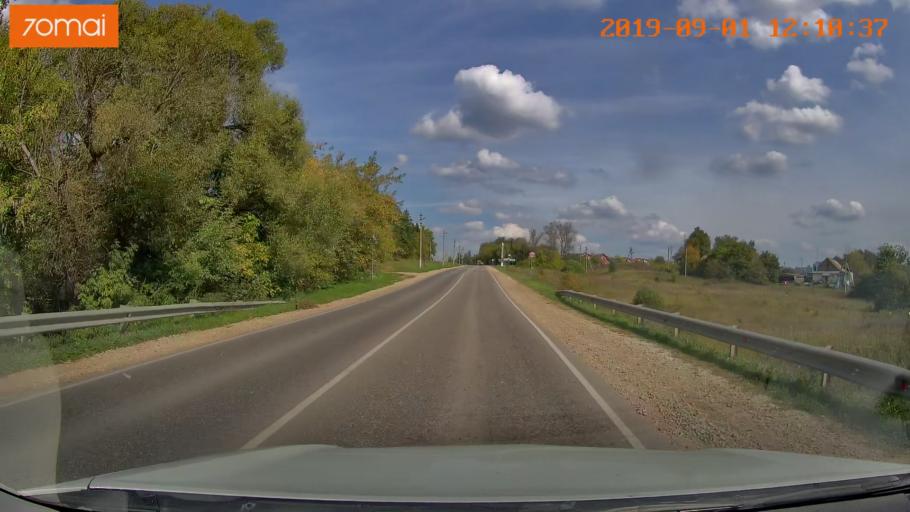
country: RU
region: Kaluga
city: Maloyaroslavets
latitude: 54.9934
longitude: 36.4341
